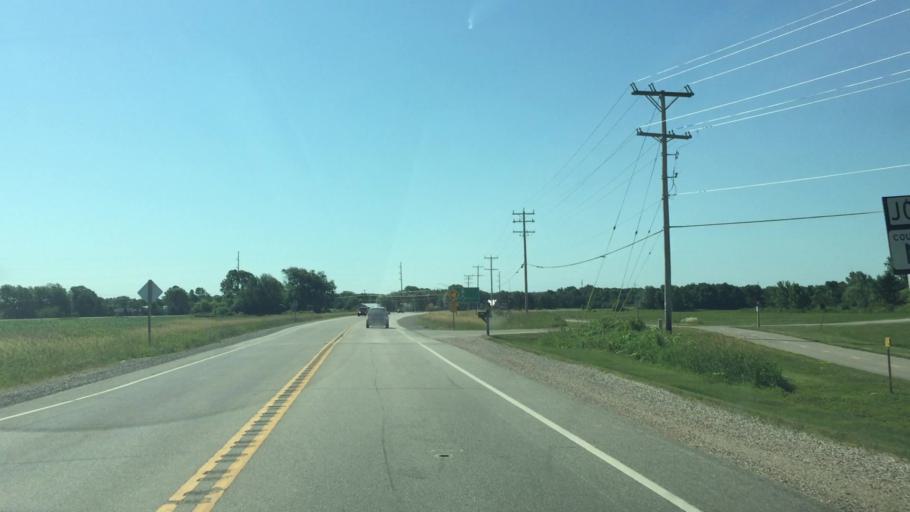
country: US
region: Wisconsin
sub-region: Outagamie County
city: Combined Locks
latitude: 44.2031
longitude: -88.3280
